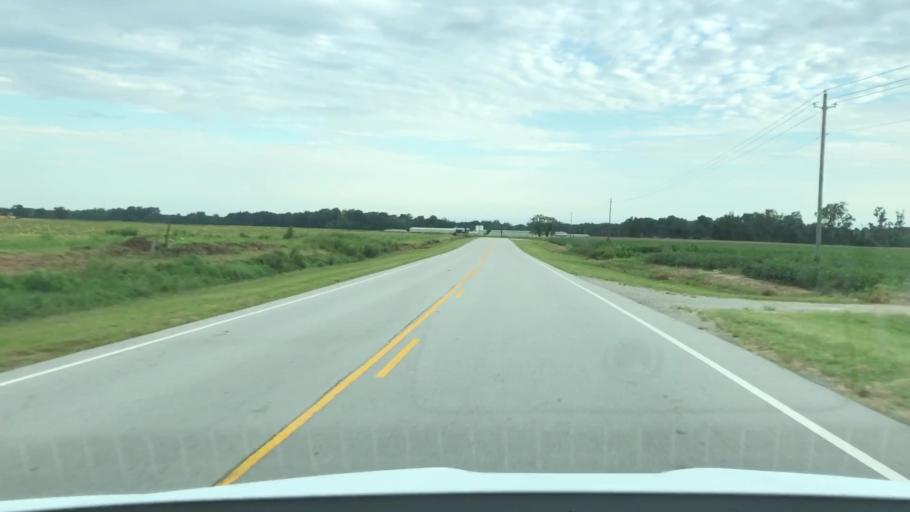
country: US
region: North Carolina
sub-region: Jones County
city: Trenton
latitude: 35.0494
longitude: -77.3534
